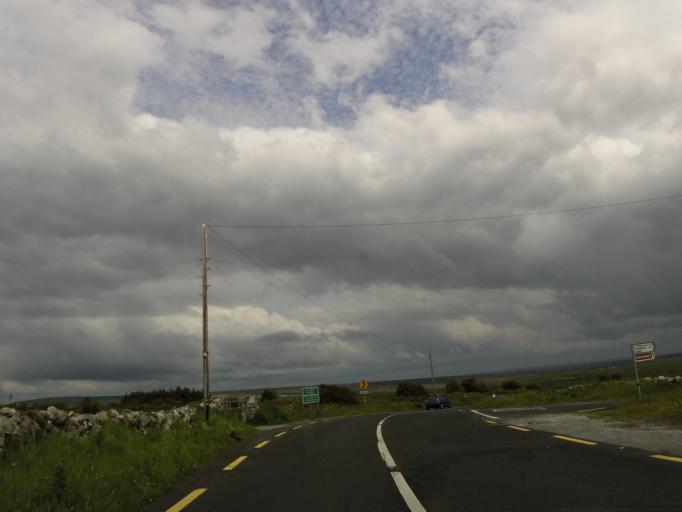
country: IE
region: Connaught
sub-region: County Galway
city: Bearna
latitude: 53.0626
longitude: -9.1963
